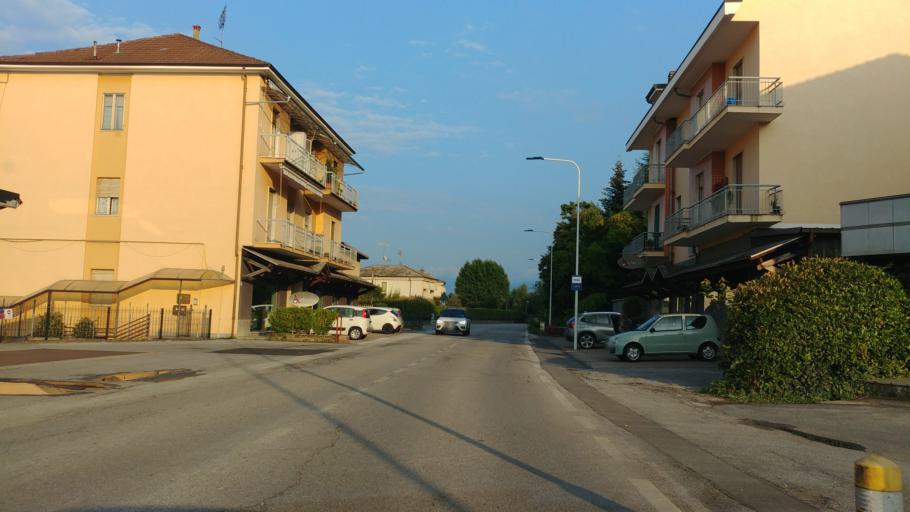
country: IT
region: Piedmont
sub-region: Provincia di Cuneo
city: Cuneo
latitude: 44.3783
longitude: 7.5724
